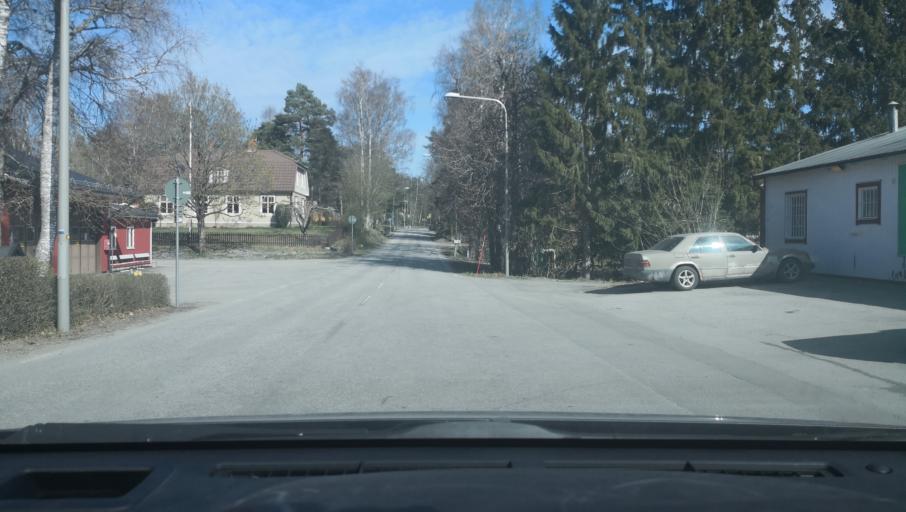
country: SE
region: Uppsala
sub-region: Enkopings Kommun
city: Irsta
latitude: 59.7770
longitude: 16.9288
